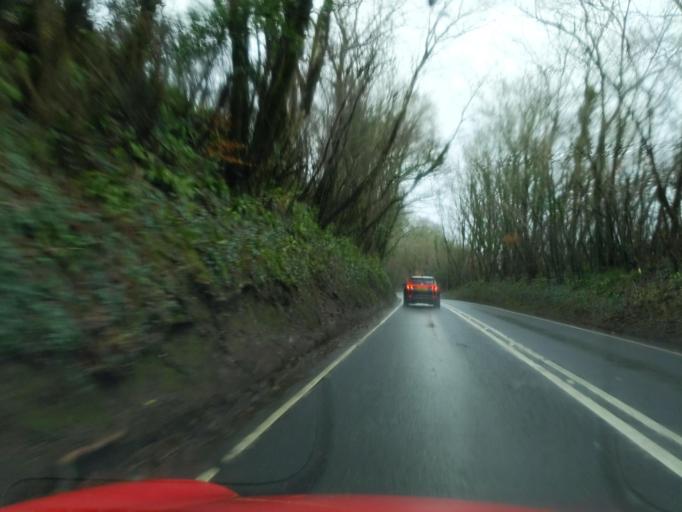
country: GB
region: England
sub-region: Cornwall
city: Launceston
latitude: 50.5875
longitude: -4.3307
